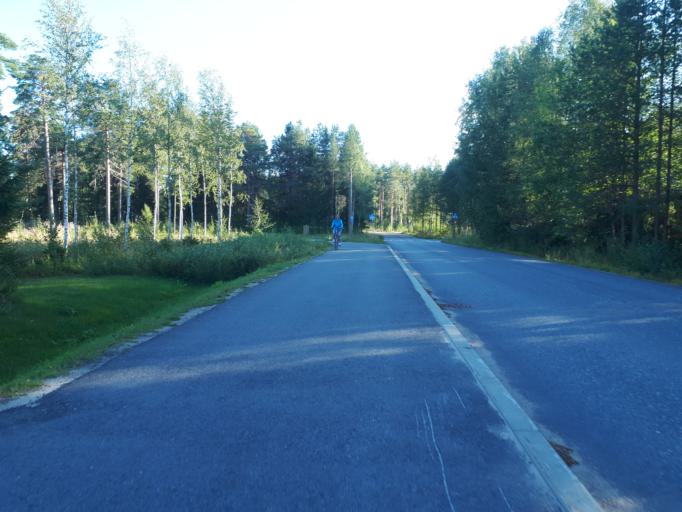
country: FI
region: Northern Ostrobothnia
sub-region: Oulunkaari
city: Ii
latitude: 65.3131
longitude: 25.3838
